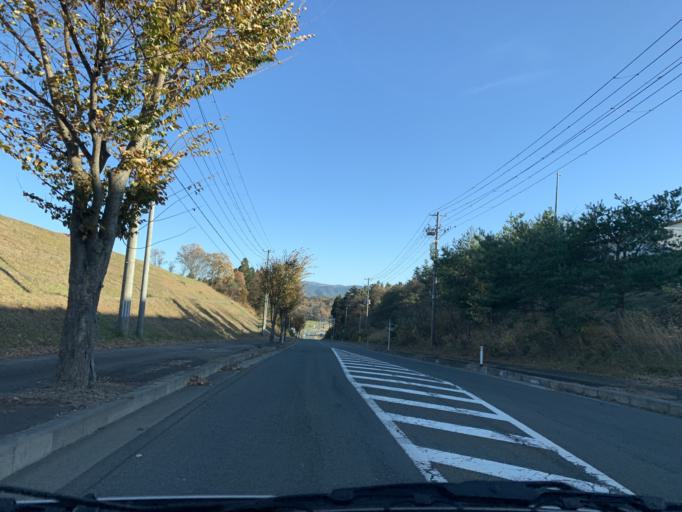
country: JP
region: Iwate
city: Mizusawa
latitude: 39.2063
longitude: 141.1830
